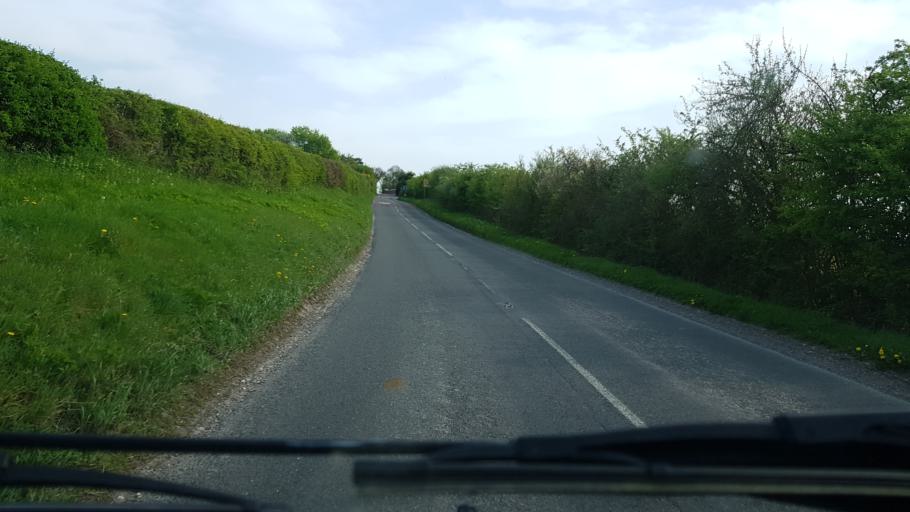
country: GB
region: England
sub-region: Hampshire
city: Overton
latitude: 51.2551
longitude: -1.2648
